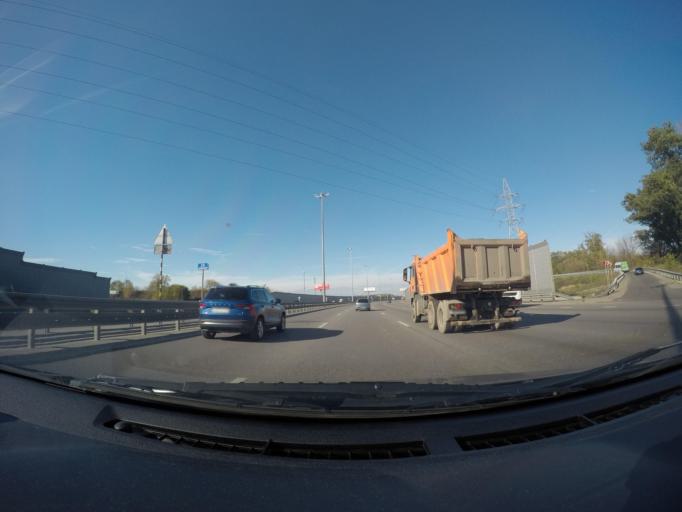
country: RU
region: Moskovskaya
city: Tomilino
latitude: 55.6334
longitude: 37.9322
